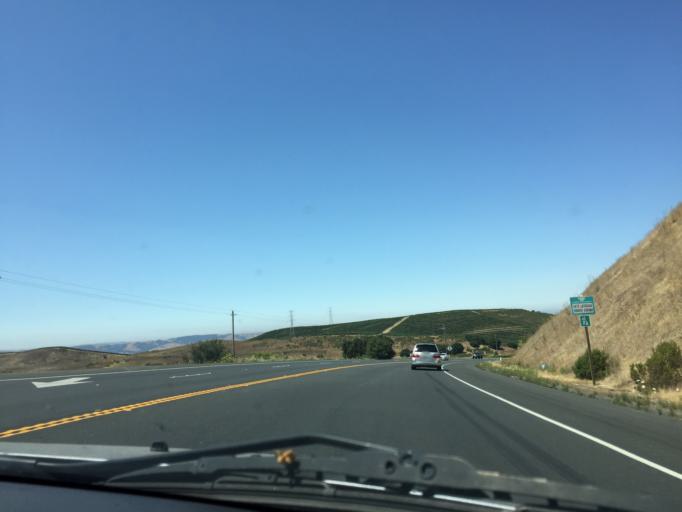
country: US
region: California
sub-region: Sonoma County
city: Sonoma
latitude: 38.2505
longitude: -122.3801
